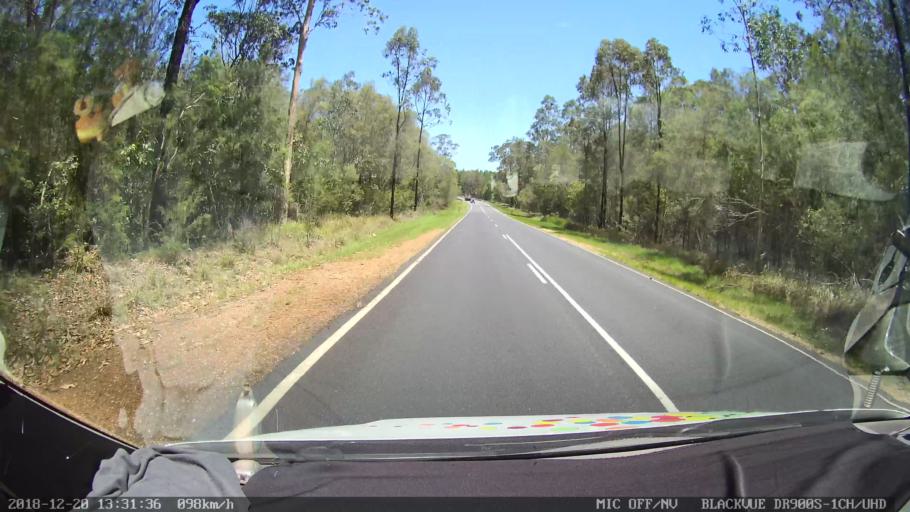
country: AU
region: New South Wales
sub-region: Clarence Valley
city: Gordon
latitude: -29.2201
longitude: 152.9883
